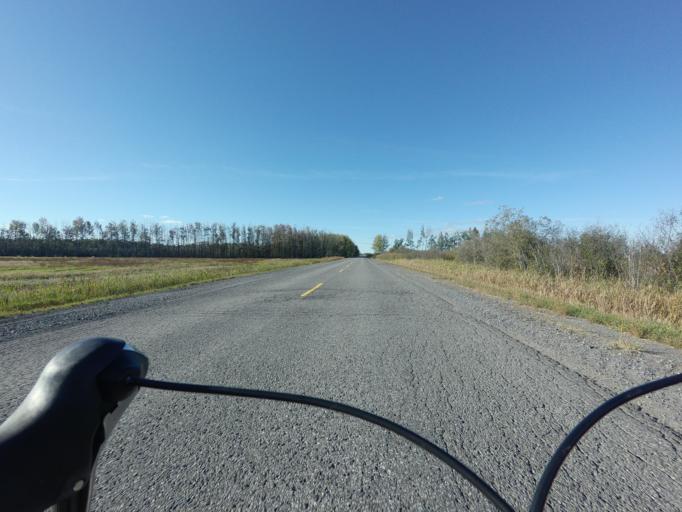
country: CA
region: Ontario
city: Bells Corners
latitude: 45.1960
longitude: -75.7880
